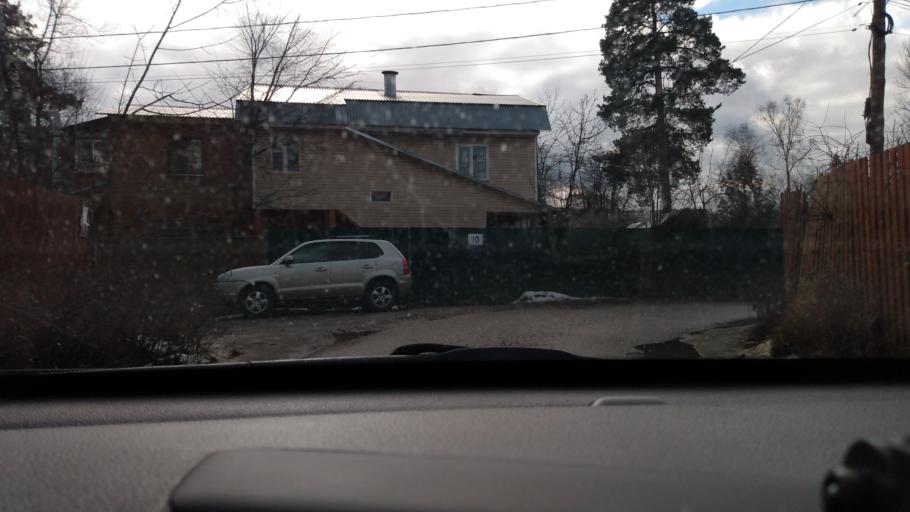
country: RU
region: Moskovskaya
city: Lesnyye Polyany
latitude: 55.9290
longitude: 37.8731
